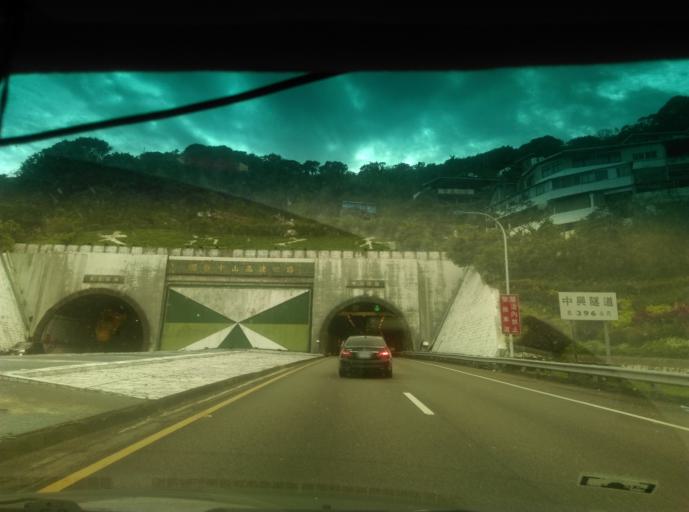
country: TW
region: Taiwan
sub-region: Keelung
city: Keelung
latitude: 25.1229
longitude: 121.7357
